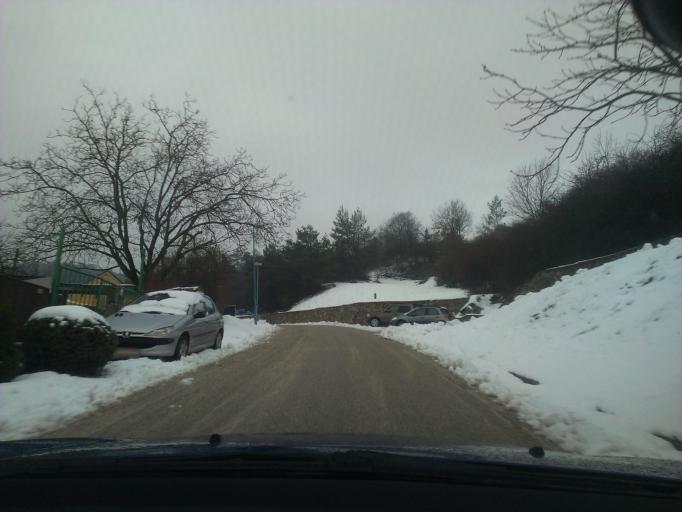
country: SK
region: Trnavsky
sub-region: Okres Trnava
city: Piestany
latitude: 48.5788
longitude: 17.8553
